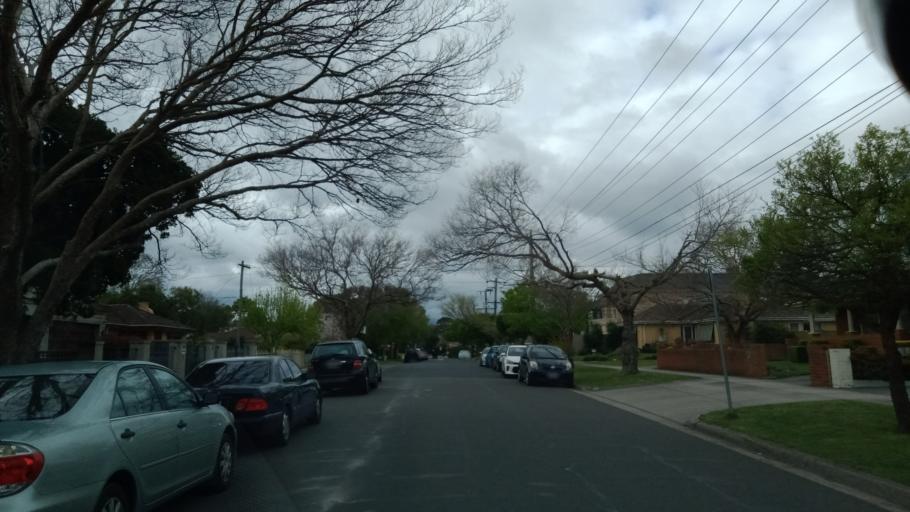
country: AU
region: Victoria
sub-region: Monash
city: Notting Hill
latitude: -37.8829
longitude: 145.1604
